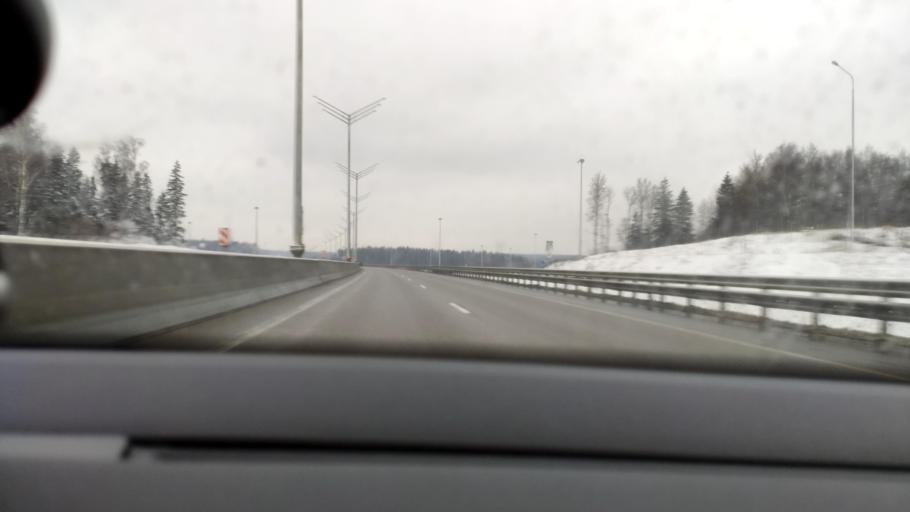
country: RU
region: Moskovskaya
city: Radumlya
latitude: 56.0970
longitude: 37.1841
